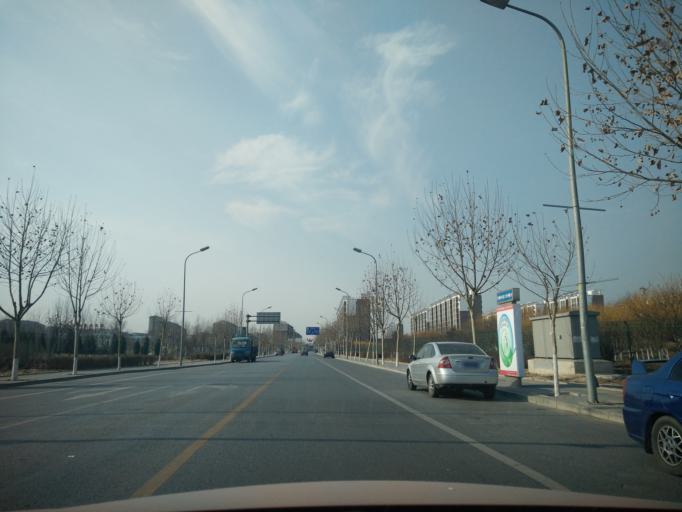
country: CN
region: Beijing
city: Yinghai
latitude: 39.7151
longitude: 116.4022
